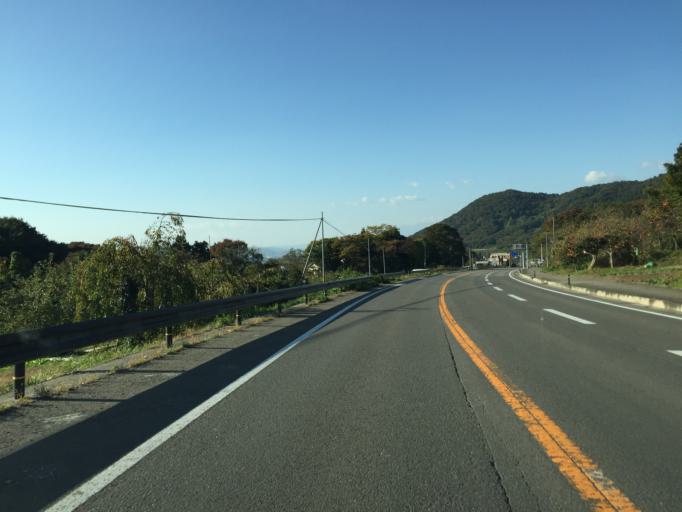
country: JP
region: Fukushima
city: Yanagawamachi-saiwaicho
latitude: 37.9042
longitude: 140.5793
